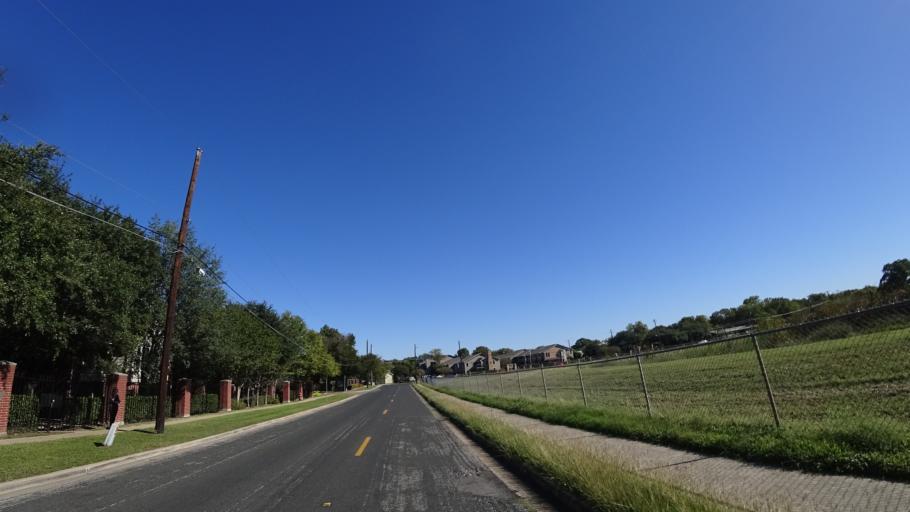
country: US
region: Texas
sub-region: Travis County
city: Rollingwood
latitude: 30.2377
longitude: -97.7877
